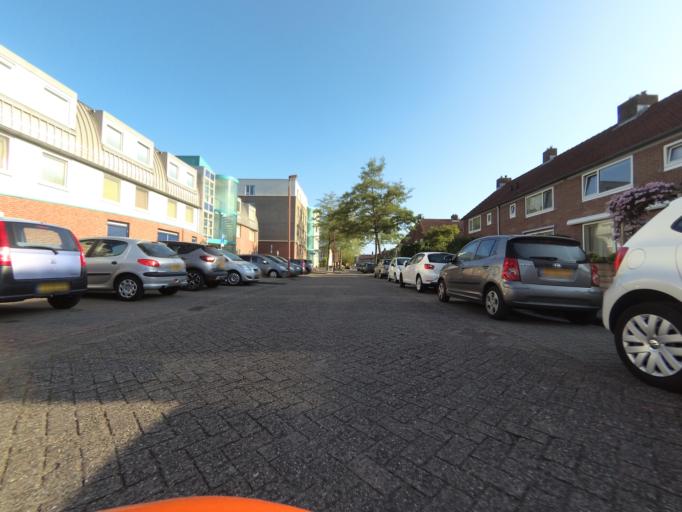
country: NL
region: Utrecht
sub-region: Gemeente Vianen
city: Vianen
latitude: 52.0064
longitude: 5.0970
